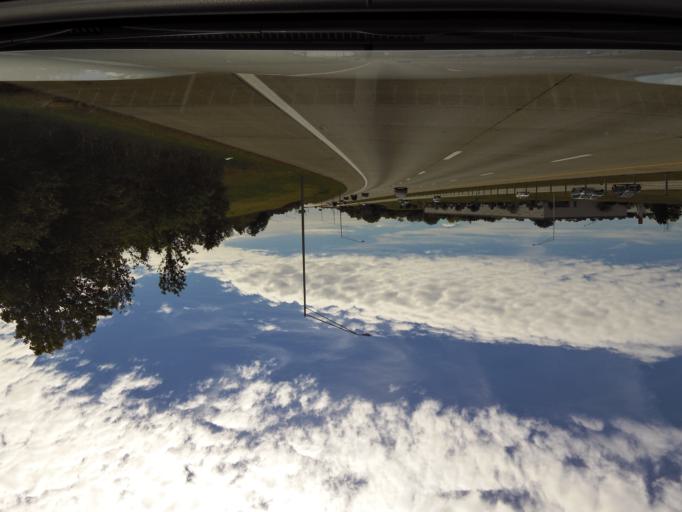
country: US
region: Kentucky
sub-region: Kenton County
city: Villa Hills
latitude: 39.0543
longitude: -84.6259
